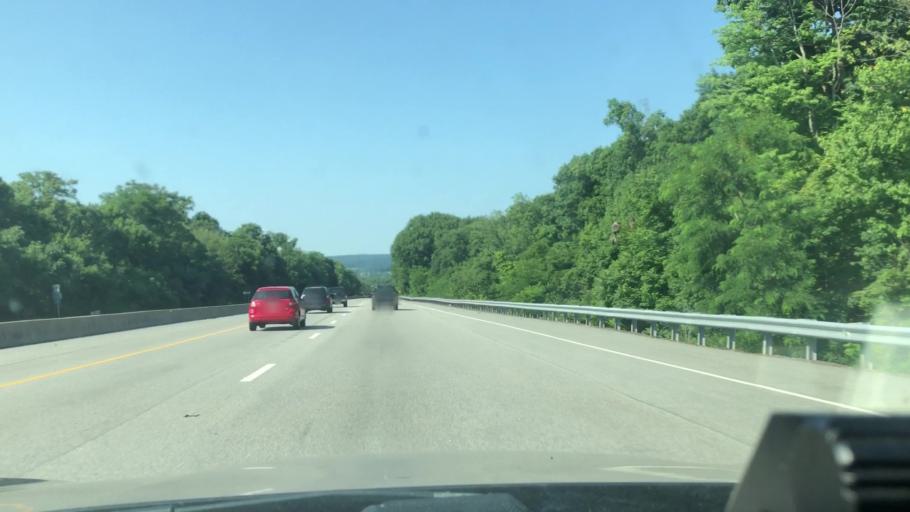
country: US
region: Pennsylvania
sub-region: Montgomery County
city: Pottstown
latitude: 40.2631
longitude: -75.6517
